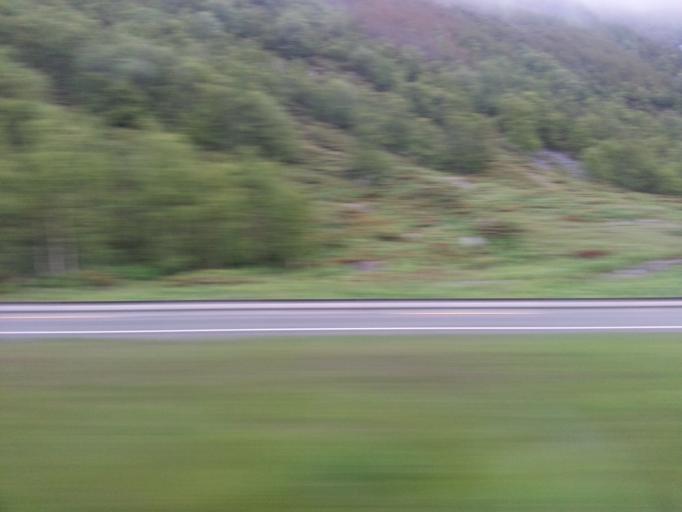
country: NO
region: Sor-Trondelag
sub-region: Oppdal
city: Oppdal
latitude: 62.4373
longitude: 9.6043
